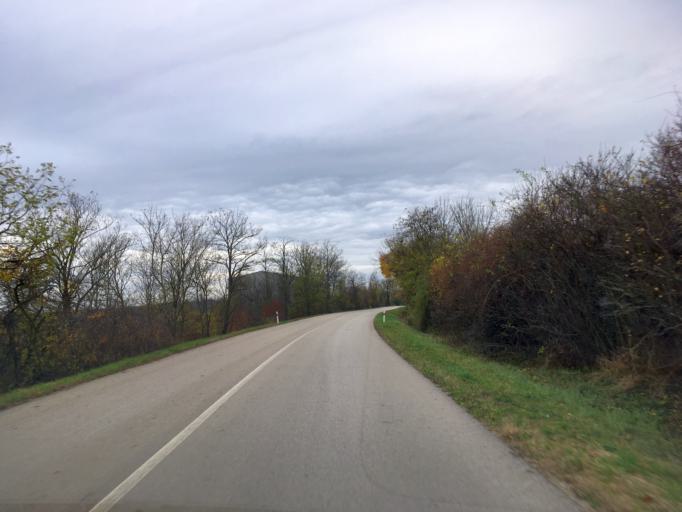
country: SK
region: Nitriansky
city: Svodin
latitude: 48.0334
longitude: 18.3817
